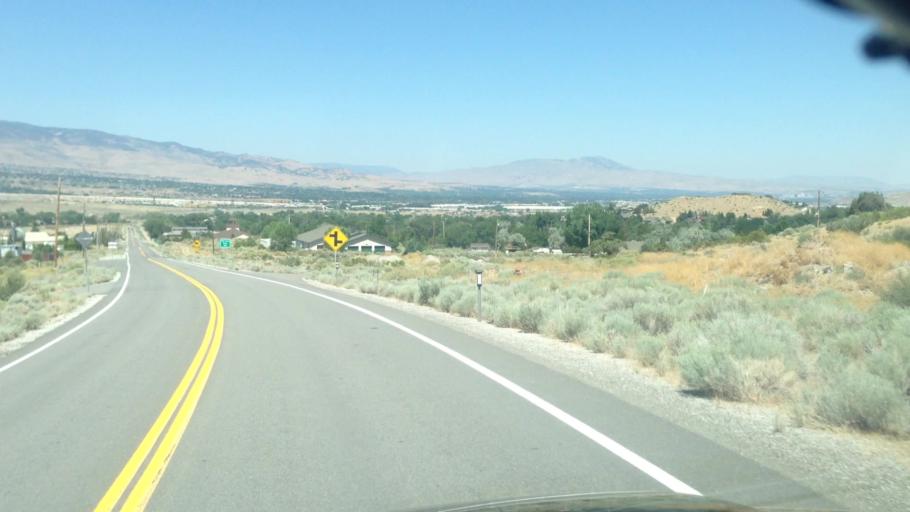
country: US
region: Nevada
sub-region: Storey County
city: Virginia City
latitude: 39.3903
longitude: -119.7163
